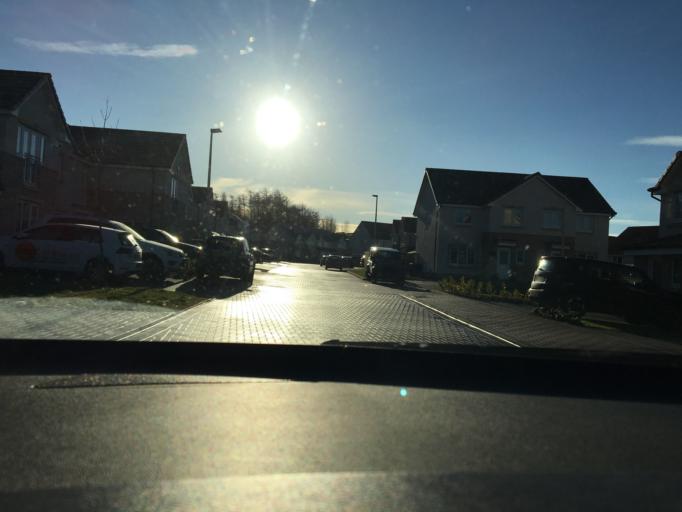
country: GB
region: Scotland
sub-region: Midlothian
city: Dalkeith
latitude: 55.8989
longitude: -3.0361
